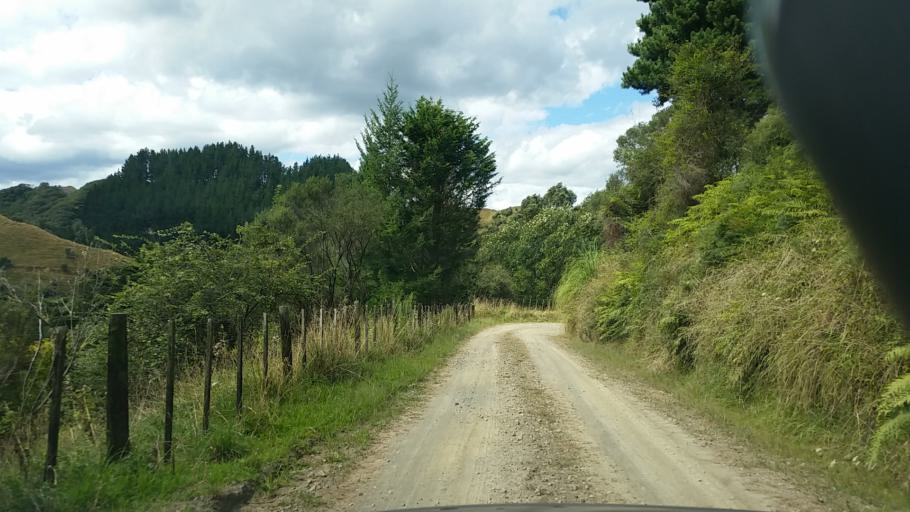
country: NZ
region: Taranaki
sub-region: South Taranaki District
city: Eltham
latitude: -39.2522
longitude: 174.5661
